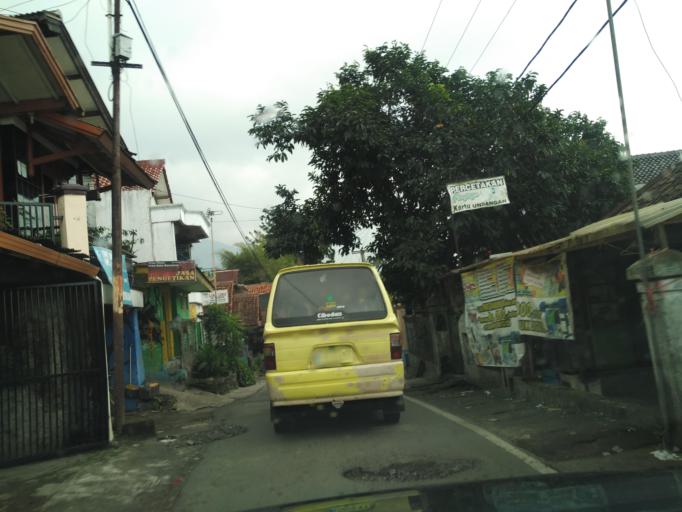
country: ID
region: West Java
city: Caringin
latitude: -6.7292
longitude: 107.0372
